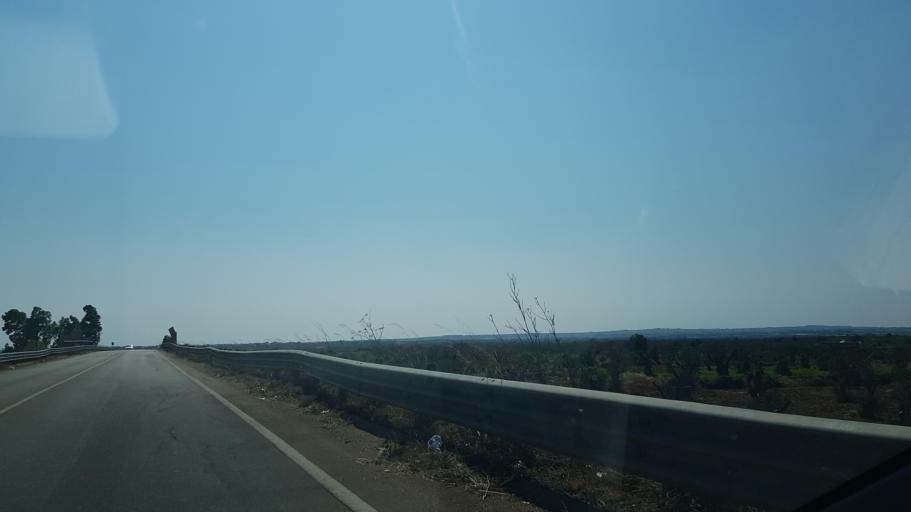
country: IT
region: Apulia
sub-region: Provincia di Lecce
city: Taurisano
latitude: 39.9462
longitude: 18.1909
